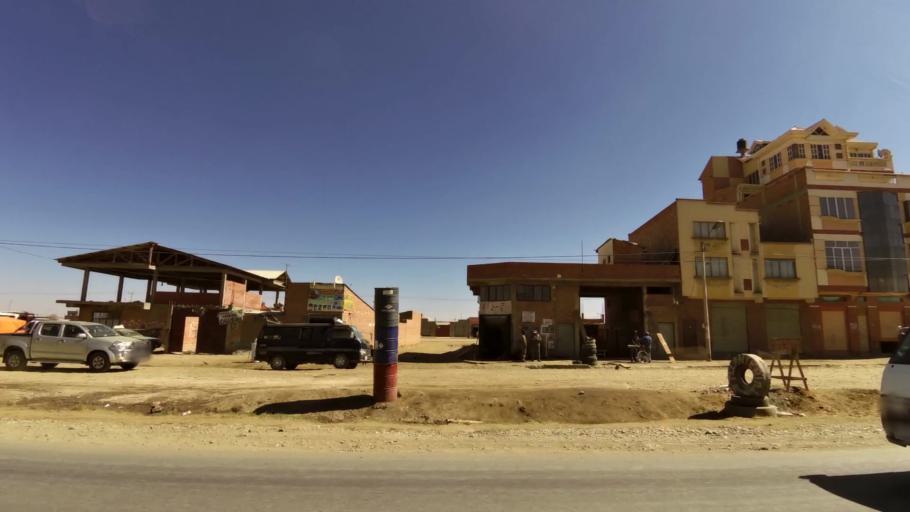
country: BO
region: La Paz
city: La Paz
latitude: -16.5600
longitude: -68.2142
